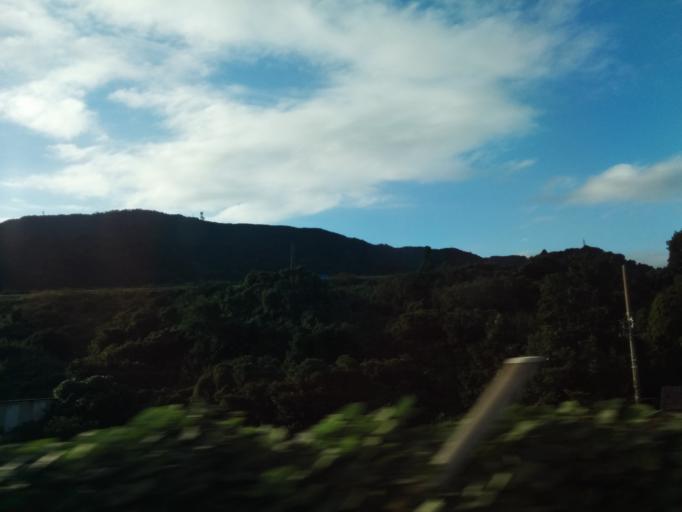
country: JP
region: Shizuoka
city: Fujinomiya
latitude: 35.1084
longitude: 138.5551
